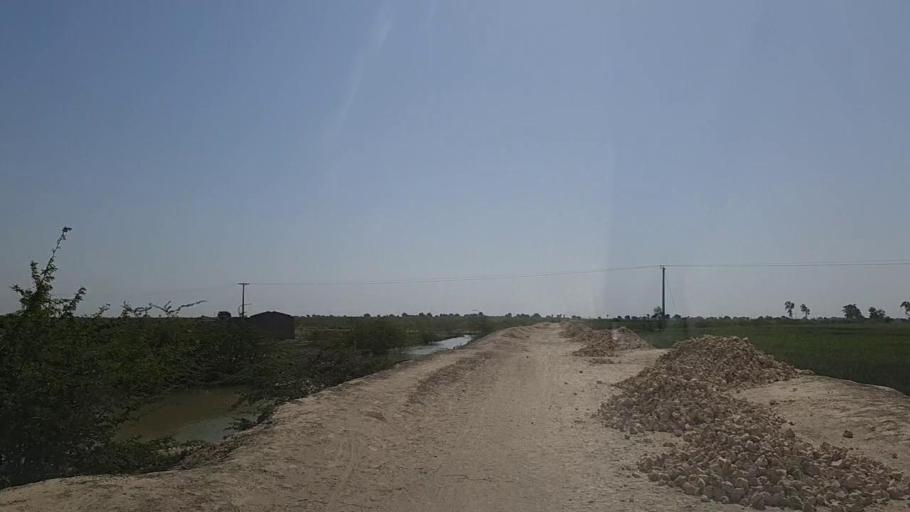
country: PK
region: Sindh
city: Samaro
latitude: 25.2298
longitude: 69.4568
